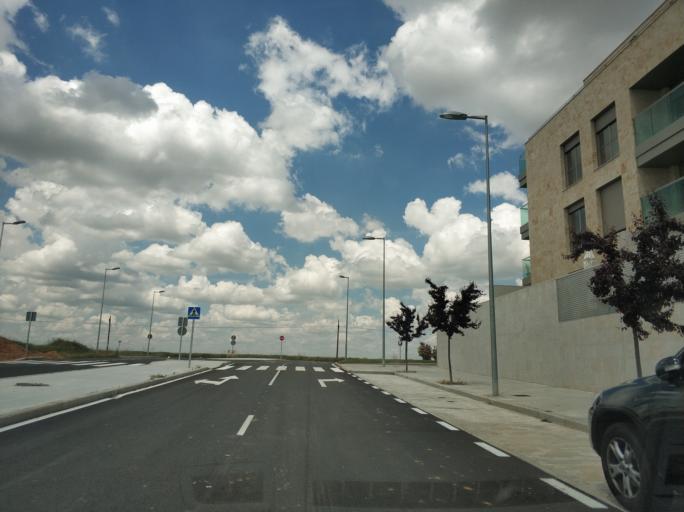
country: ES
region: Castille and Leon
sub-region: Provincia de Salamanca
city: Aldeatejada
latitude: 40.9457
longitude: -5.6847
